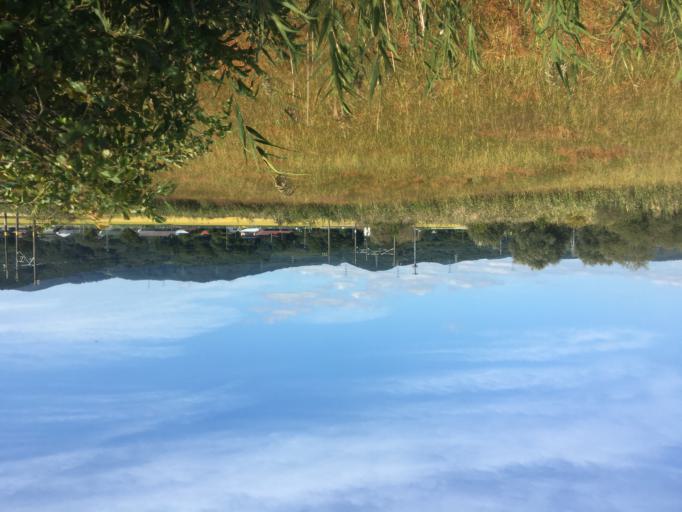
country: JP
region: Iwate
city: Morioka-shi
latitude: 39.8795
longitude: 141.1766
